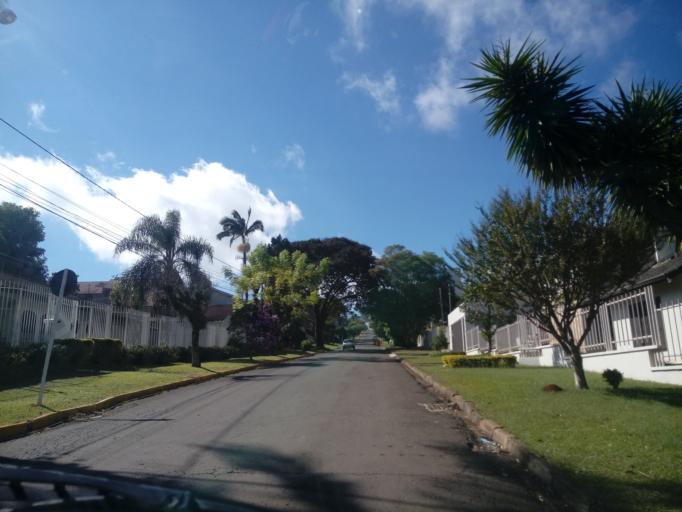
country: BR
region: Santa Catarina
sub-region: Chapeco
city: Chapeco
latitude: -27.1148
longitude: -52.6151
